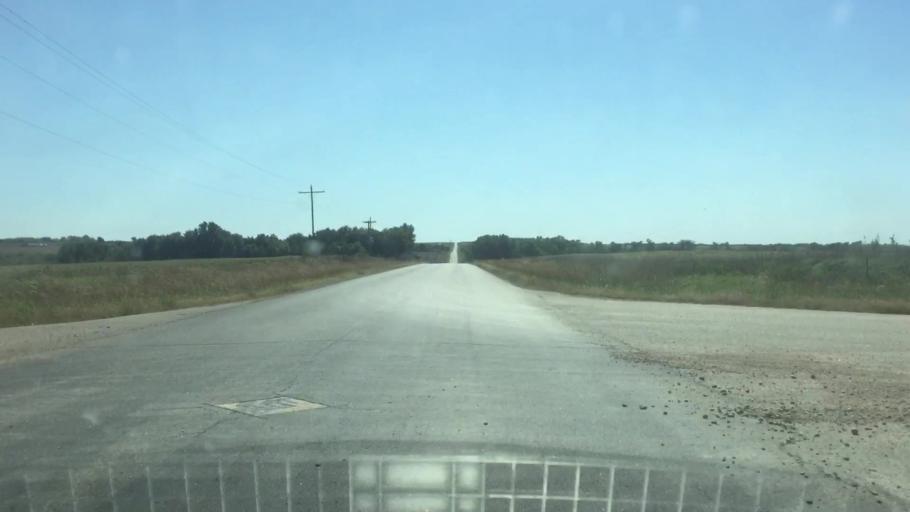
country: US
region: Kansas
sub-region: Marshall County
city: Marysville
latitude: 39.9431
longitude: -96.6008
